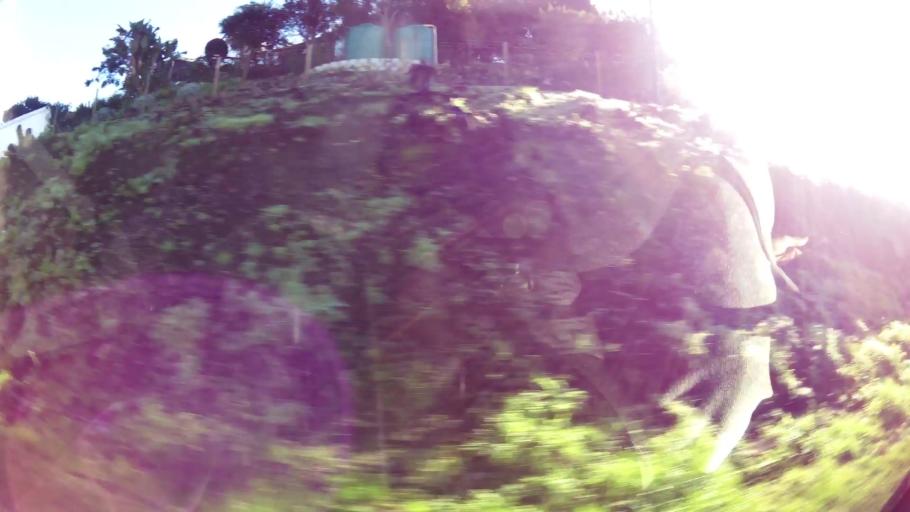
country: ZA
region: Western Cape
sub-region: Eden District Municipality
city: Knysna
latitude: -34.0347
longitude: 23.0166
